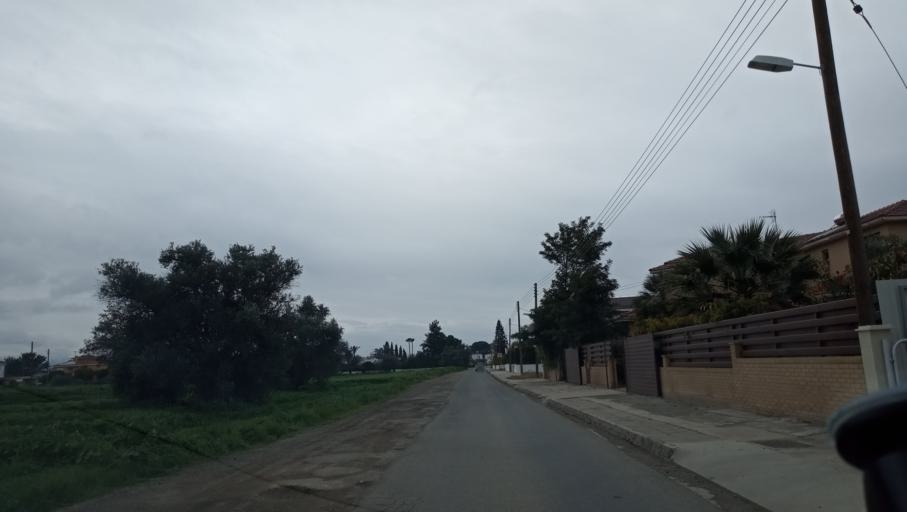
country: CY
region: Lefkosia
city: Pano Deftera
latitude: 35.0774
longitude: 33.2695
